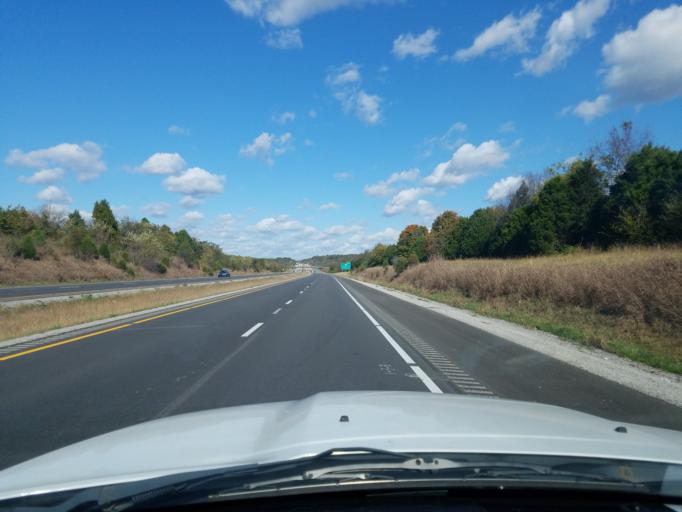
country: US
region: Kentucky
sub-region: Warren County
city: Bowling Green
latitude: 36.9838
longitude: -86.5020
